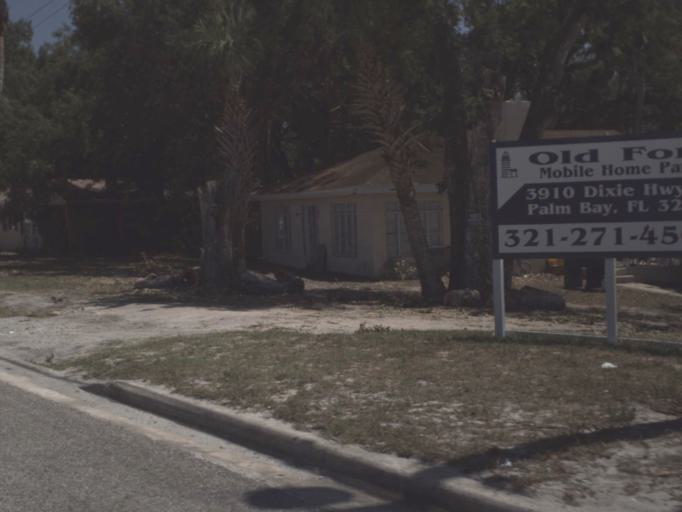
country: US
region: Florida
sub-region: Brevard County
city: Palm Bay
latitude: 28.0421
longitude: -80.5835
